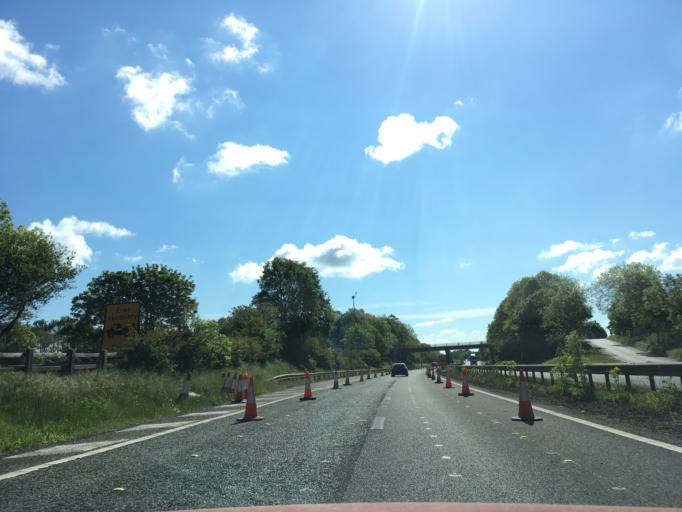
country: GB
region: England
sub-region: Herefordshire
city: Donnington
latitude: 51.9971
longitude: -2.3625
